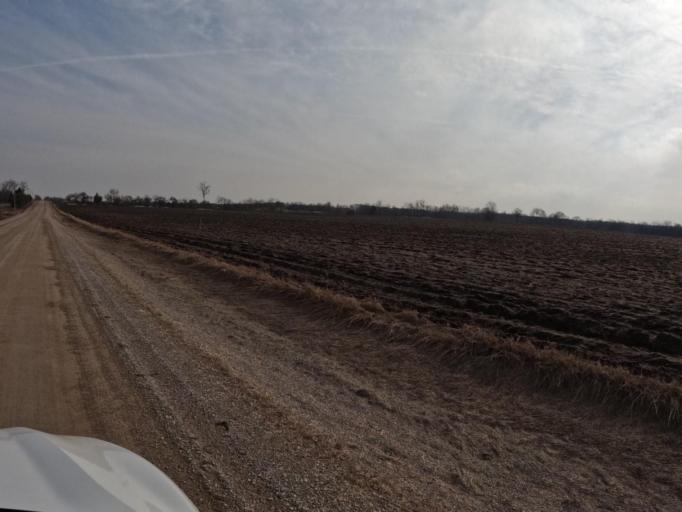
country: CA
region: Ontario
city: Orangeville
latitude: 43.9087
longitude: -80.2698
